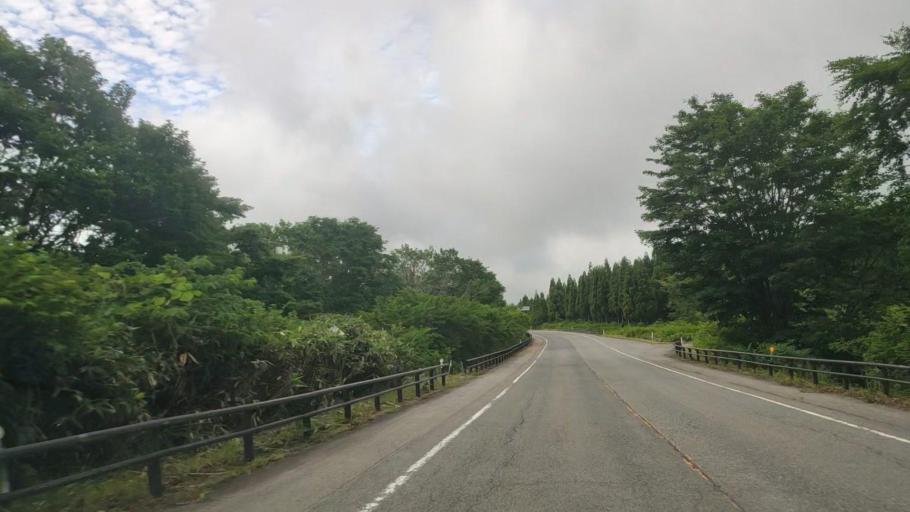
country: JP
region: Tottori
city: Kurayoshi
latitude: 35.3397
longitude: 133.5812
